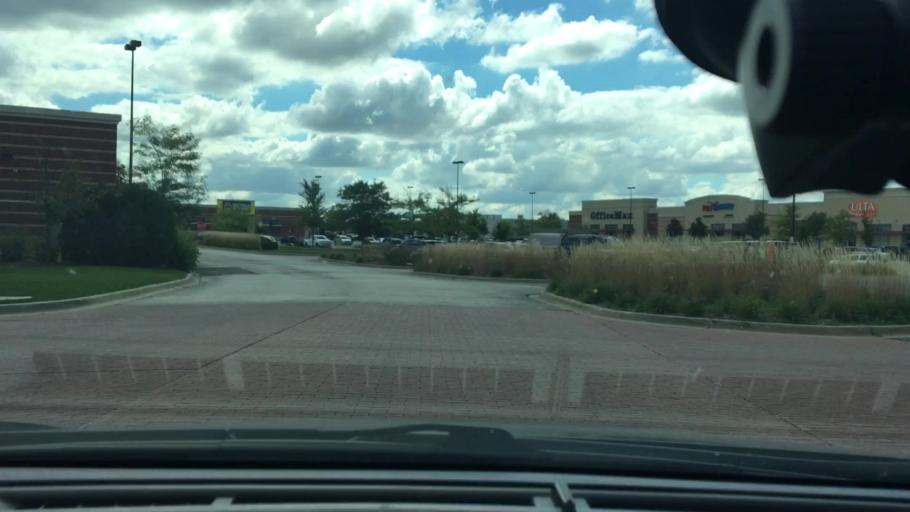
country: US
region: Illinois
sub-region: Cook County
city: Streamwood
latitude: 42.0725
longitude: -88.1917
